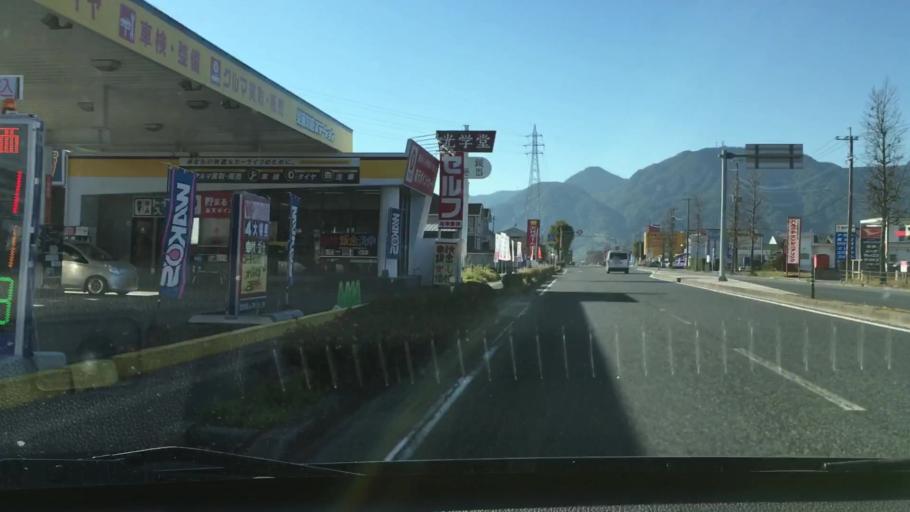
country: JP
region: Kagoshima
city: Kajiki
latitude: 31.7255
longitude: 130.6239
